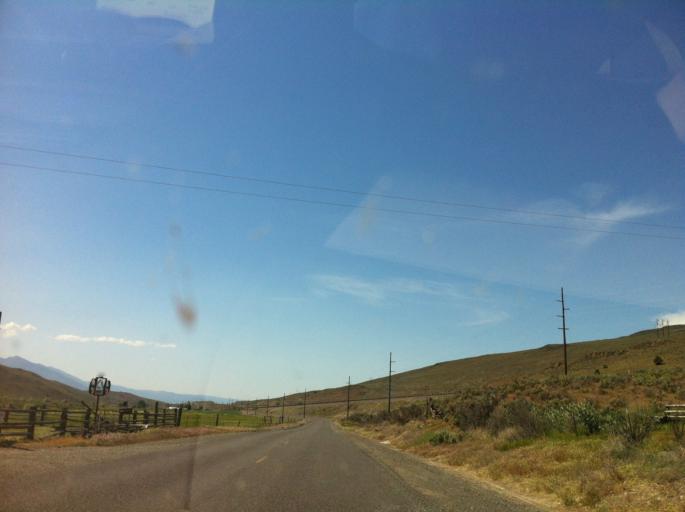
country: US
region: Oregon
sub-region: Baker County
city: Baker City
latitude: 44.7126
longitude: -117.7722
